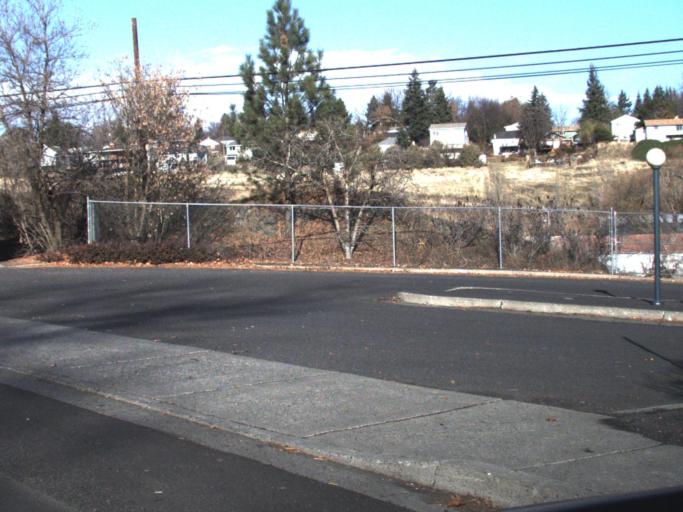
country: US
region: Washington
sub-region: Whitman County
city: Pullman
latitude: 46.7312
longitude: -117.1813
